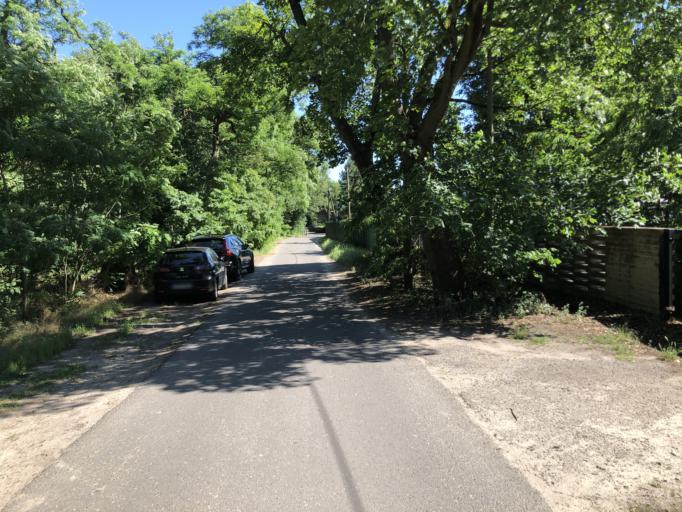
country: DE
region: Berlin
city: Friedrichshagen
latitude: 52.4814
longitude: 13.6356
